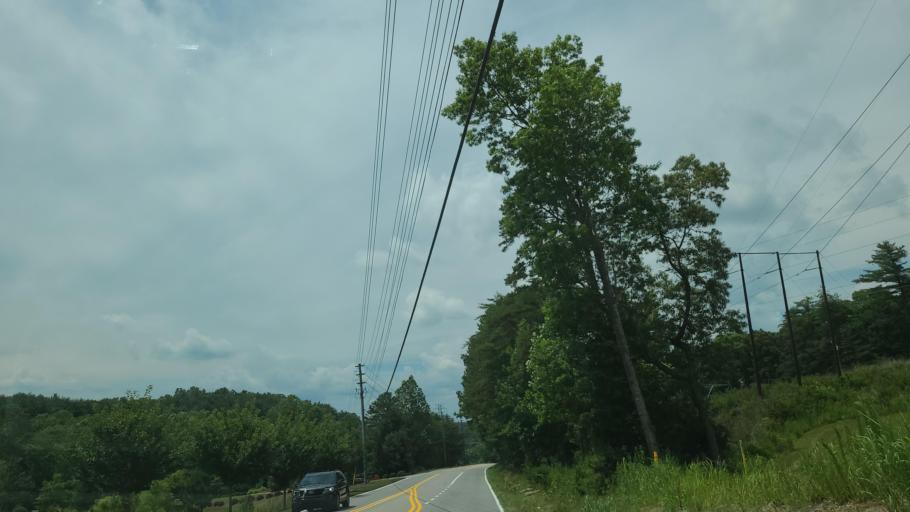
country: US
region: North Carolina
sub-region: Buncombe County
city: Avery Creek
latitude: 35.4833
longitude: -82.5691
